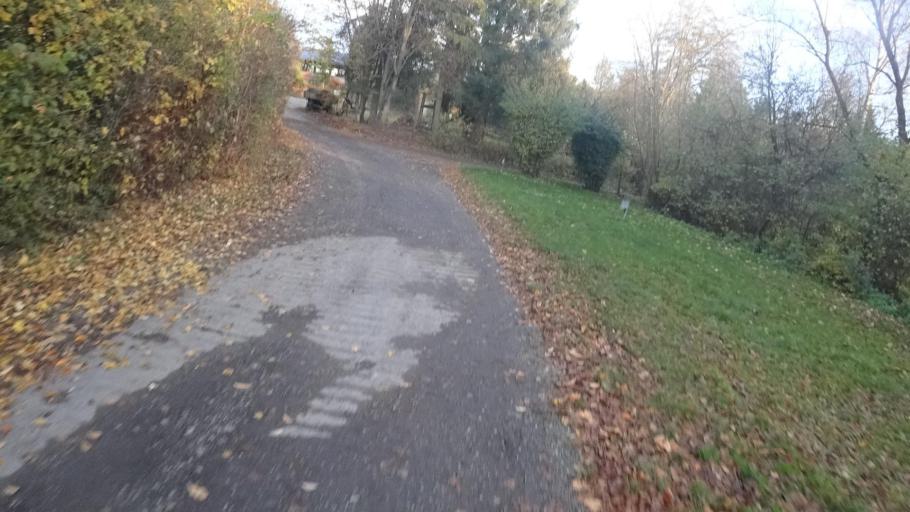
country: DE
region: Rheinland-Pfalz
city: Hausbay
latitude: 50.1048
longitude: 7.5658
